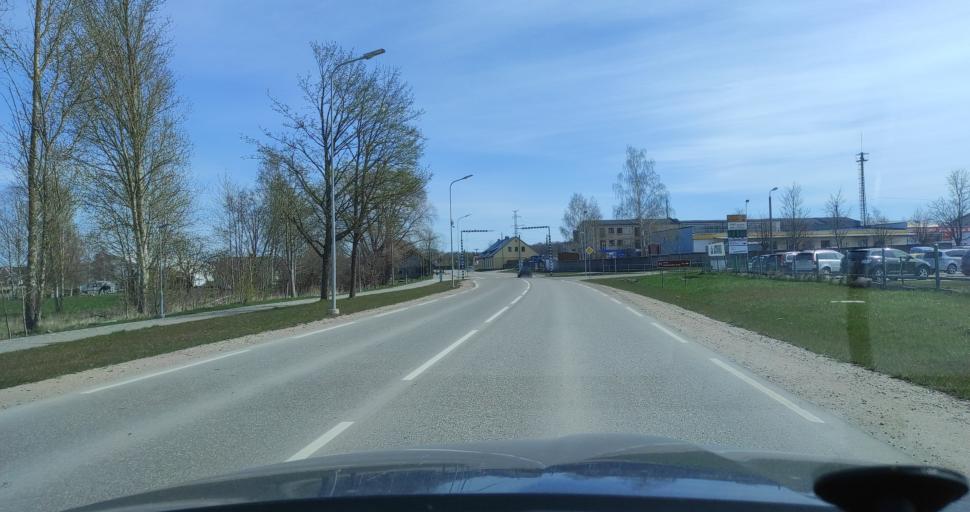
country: LV
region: Talsu Rajons
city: Talsi
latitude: 57.2337
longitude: 22.5616
